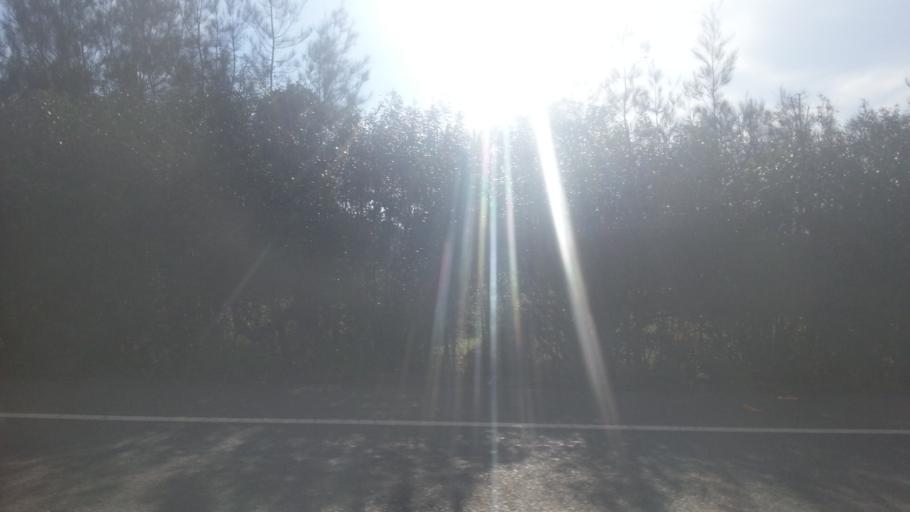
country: AU
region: New South Wales
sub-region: Liverpool
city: Luddenham
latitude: -33.9021
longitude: 150.7042
